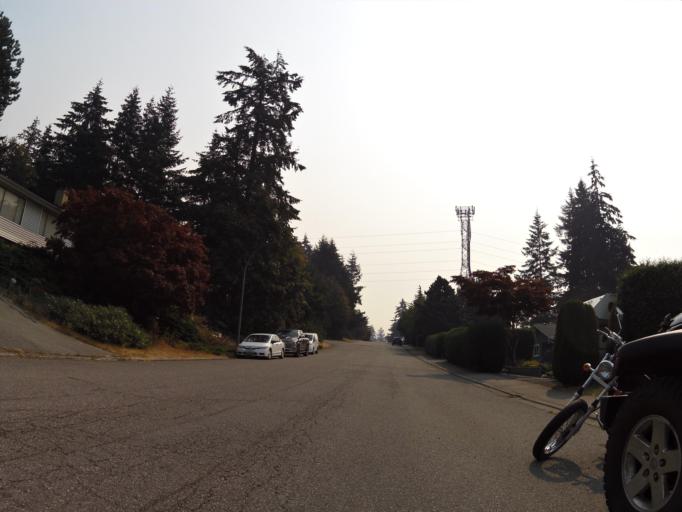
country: CA
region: British Columbia
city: Delta
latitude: 49.1507
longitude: -122.9287
